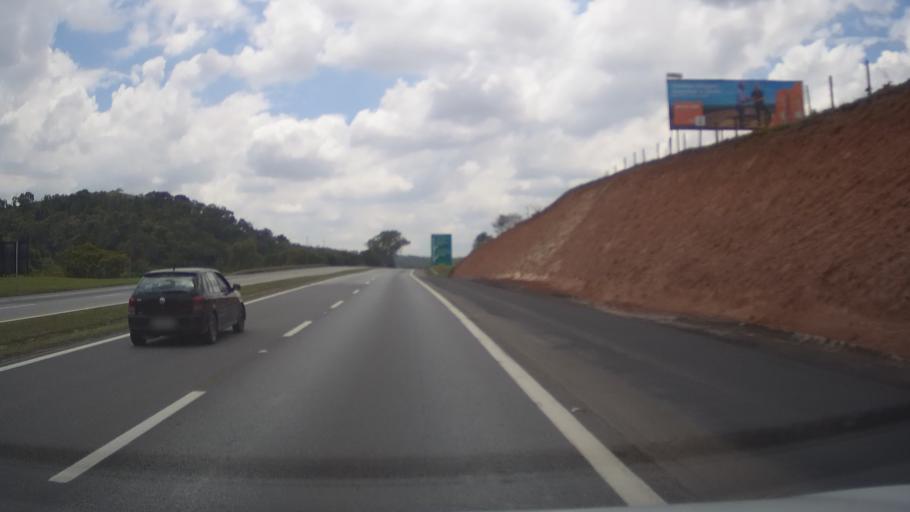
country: BR
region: Minas Gerais
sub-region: Tres Coracoes
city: Tres Coracoes
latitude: -21.6818
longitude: -45.3427
